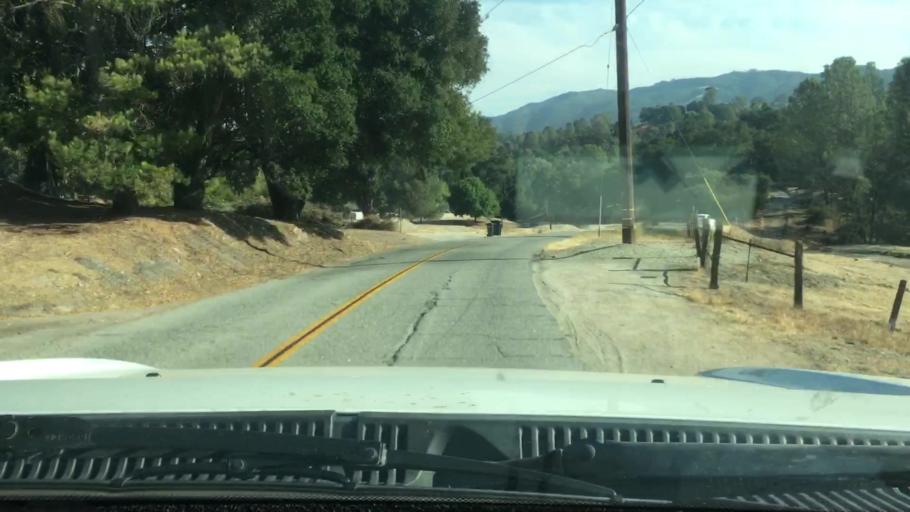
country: US
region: California
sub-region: San Luis Obispo County
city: Atascadero
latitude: 35.4549
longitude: -120.6541
